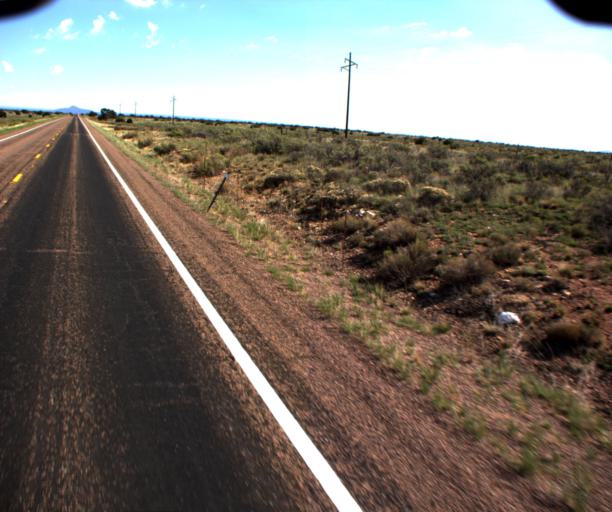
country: US
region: Arizona
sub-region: Coconino County
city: Williams
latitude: 35.5776
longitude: -112.1532
